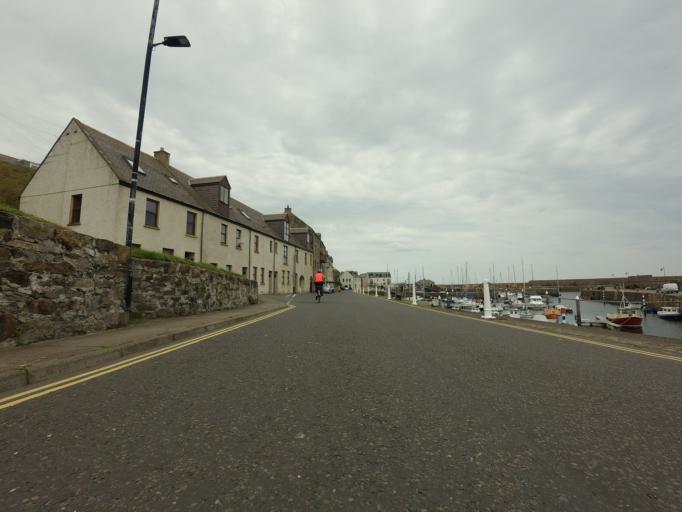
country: GB
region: Scotland
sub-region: Aberdeenshire
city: Banff
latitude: 57.6688
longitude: -2.5226
